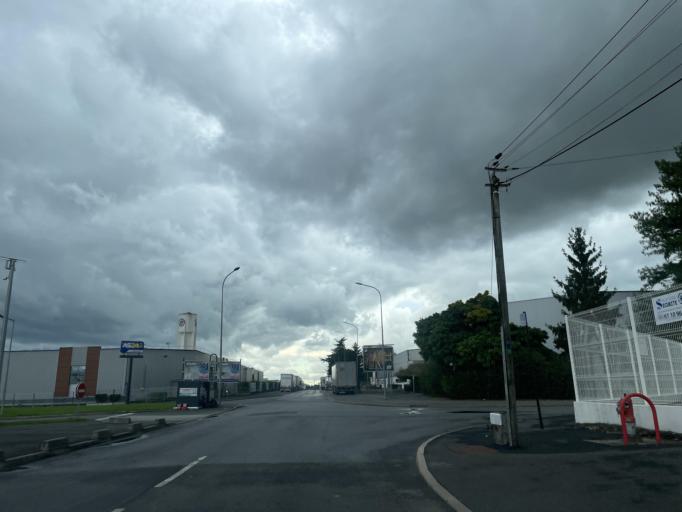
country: FR
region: Ile-de-France
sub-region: Departement de Seine-et-Marne
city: Fublaines
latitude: 48.9599
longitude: 2.9182
